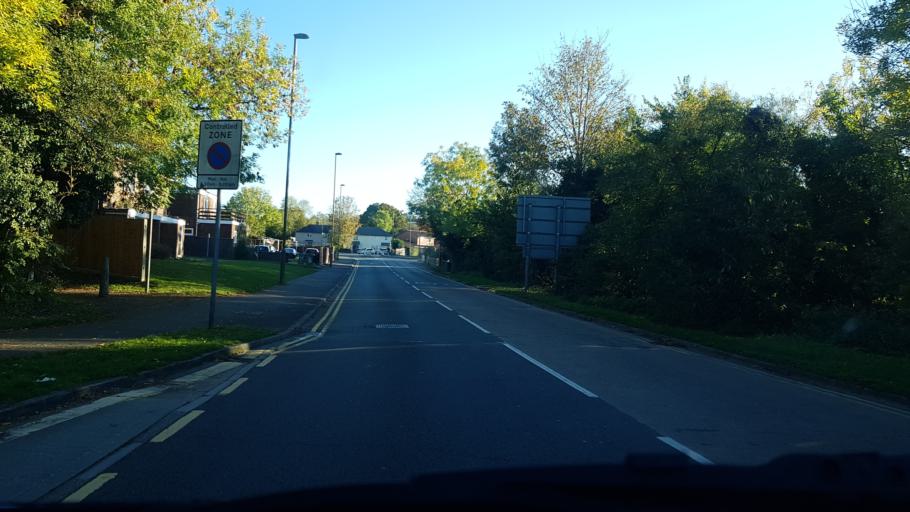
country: GB
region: England
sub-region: Surrey
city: Guildford
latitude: 51.2409
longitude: -0.5954
